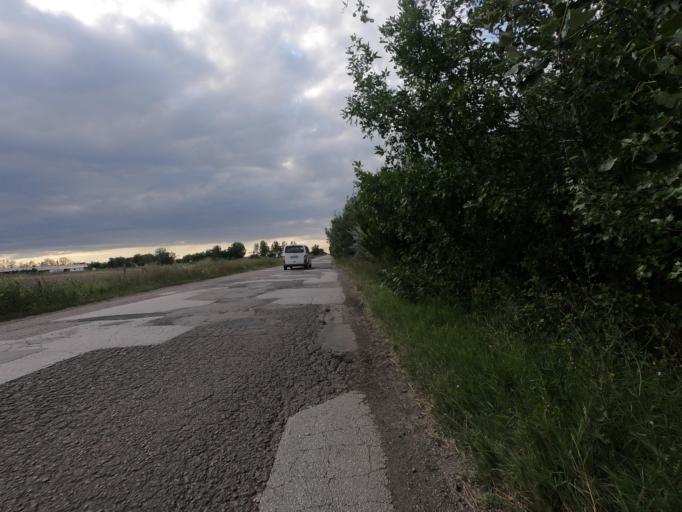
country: HU
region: Heves
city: Poroszlo
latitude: 47.6718
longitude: 20.6623
